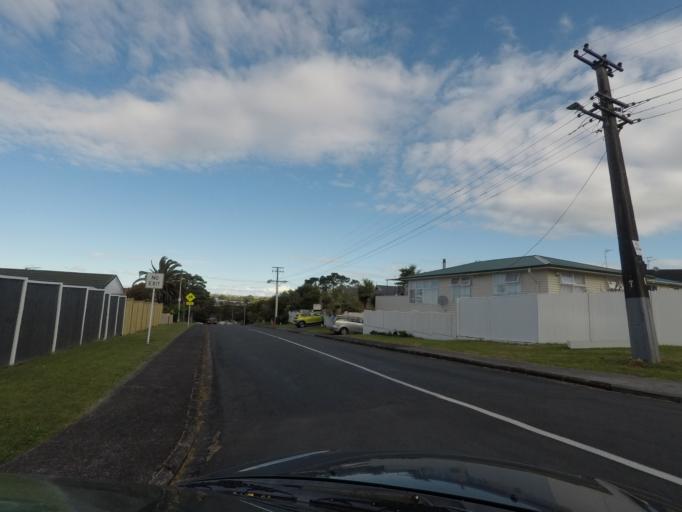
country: NZ
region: Auckland
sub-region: Auckland
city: Rosebank
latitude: -36.8838
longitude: 174.6516
